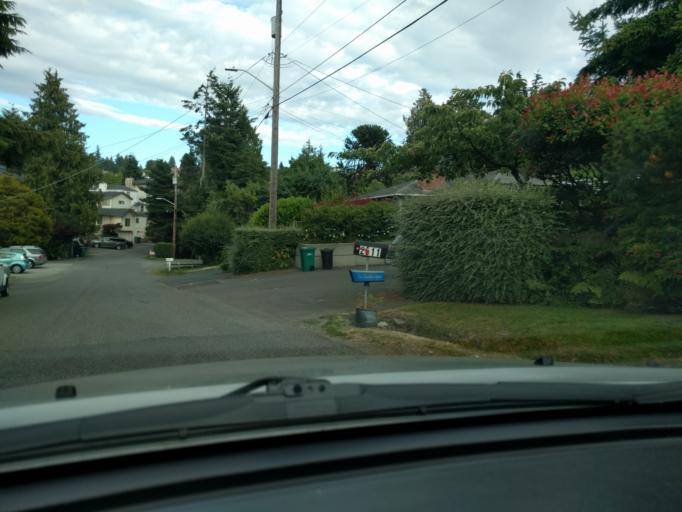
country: US
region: Washington
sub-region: King County
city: Shoreline
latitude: 47.7008
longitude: -122.3909
